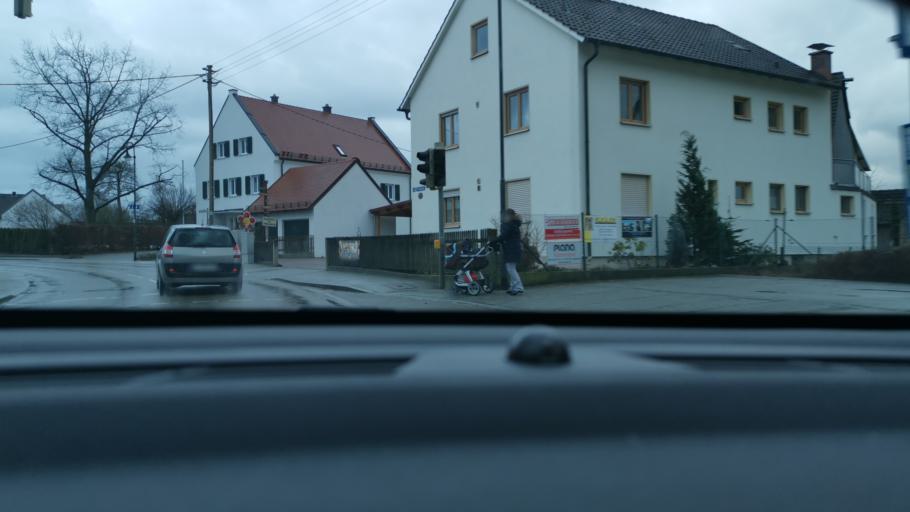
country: DE
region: Bavaria
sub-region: Swabia
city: Affing
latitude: 48.4584
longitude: 10.9814
